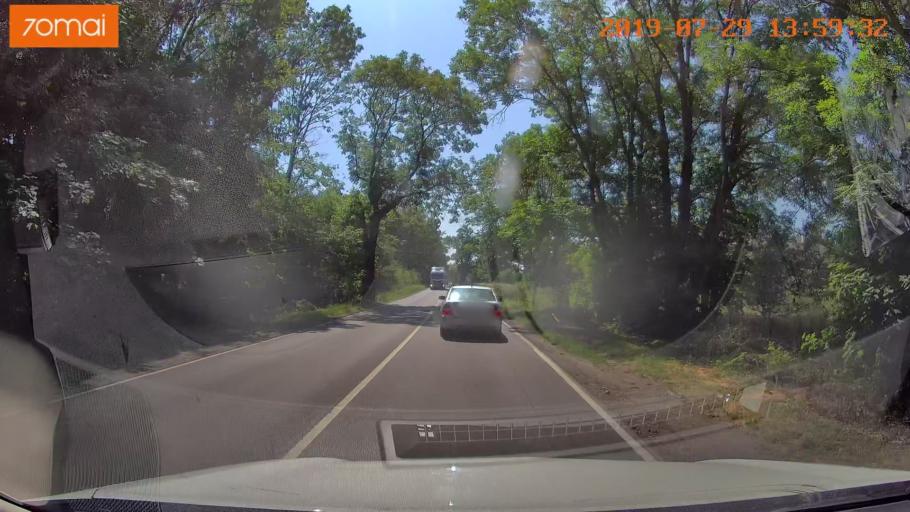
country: RU
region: Kaliningrad
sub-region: Gorod Kaliningrad
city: Baltiysk
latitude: 54.6844
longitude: 19.9319
